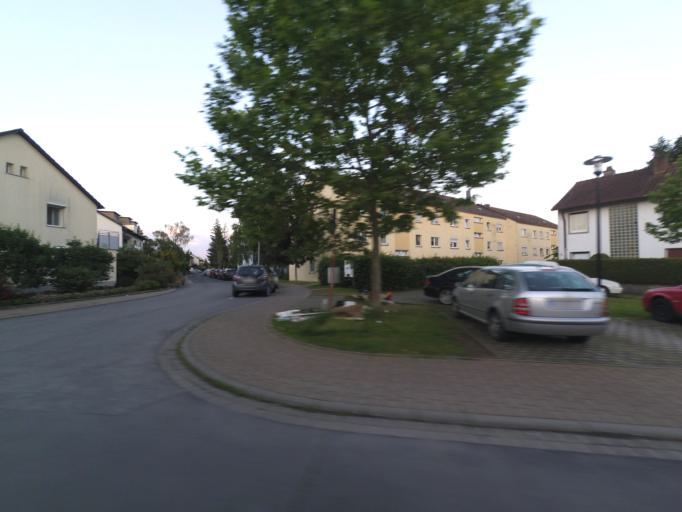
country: DE
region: Bavaria
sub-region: Regierungsbezirk Unterfranken
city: Hassfurt
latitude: 50.0366
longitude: 10.5221
